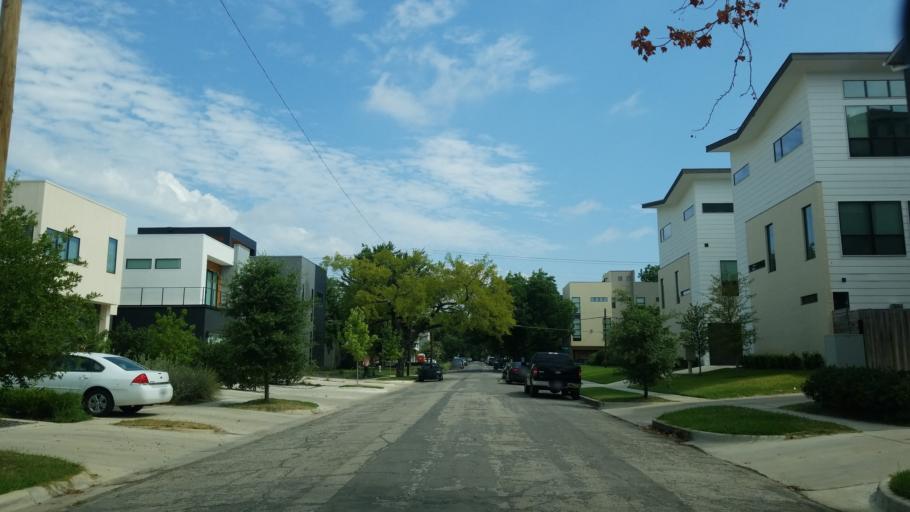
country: US
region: Texas
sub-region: Dallas County
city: Highland Park
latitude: 32.8127
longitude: -96.7735
